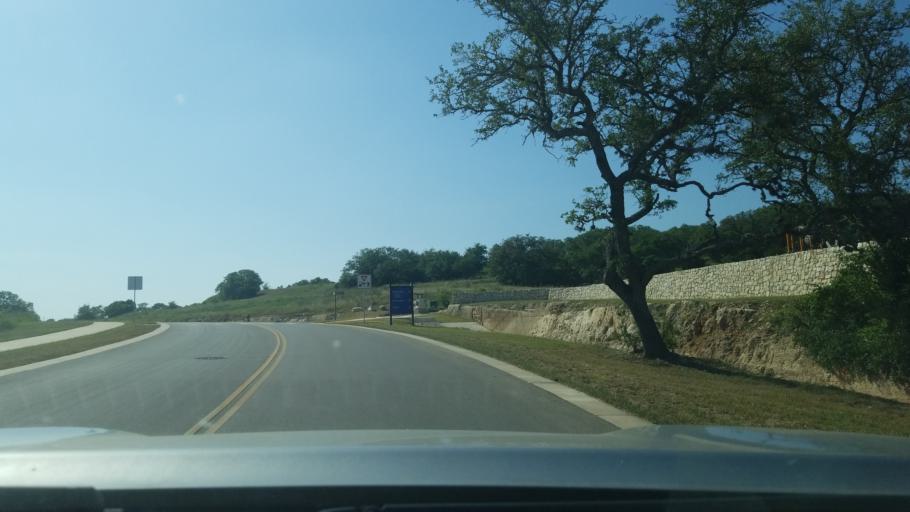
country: US
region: Texas
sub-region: Comal County
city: Bulverde
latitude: 29.7612
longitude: -98.4228
